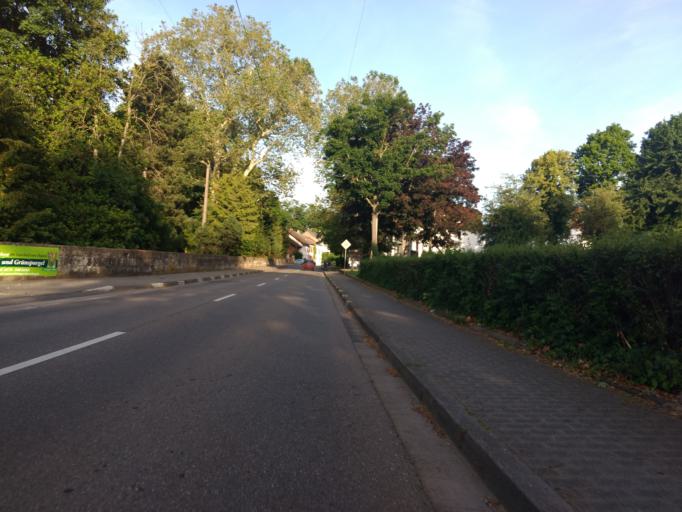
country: DE
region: Saarland
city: Wallerfangen
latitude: 49.3282
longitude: 6.7199
